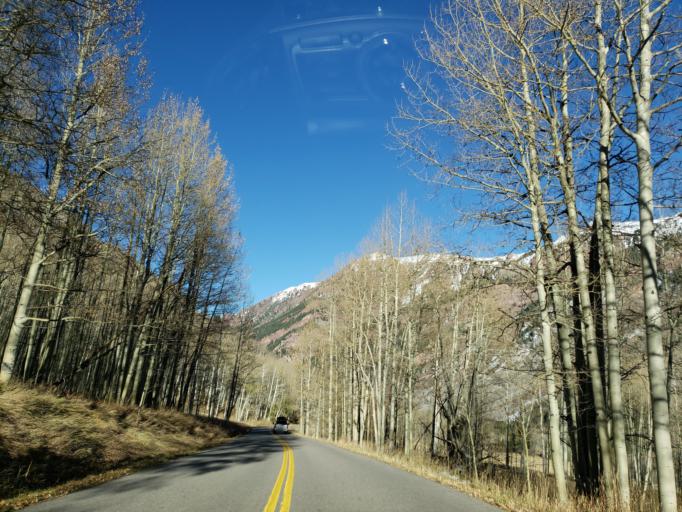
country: US
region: Colorado
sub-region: Pitkin County
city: Snowmass Village
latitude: 39.1058
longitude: -106.9244
